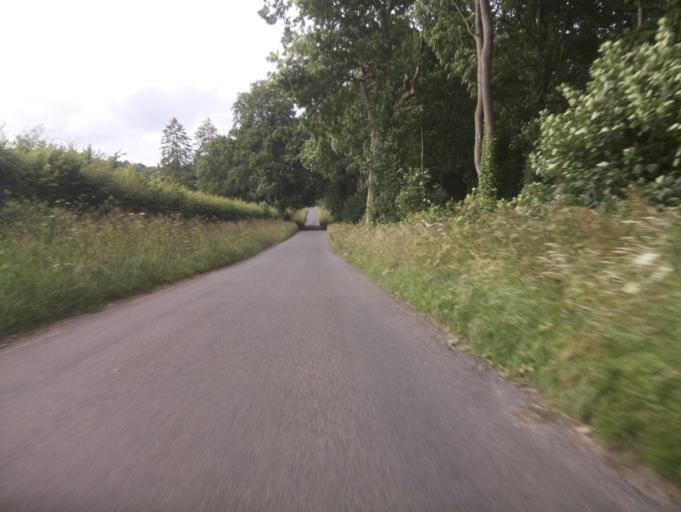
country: GB
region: England
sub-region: Gloucestershire
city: Donnington
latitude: 51.9777
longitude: -1.7550
